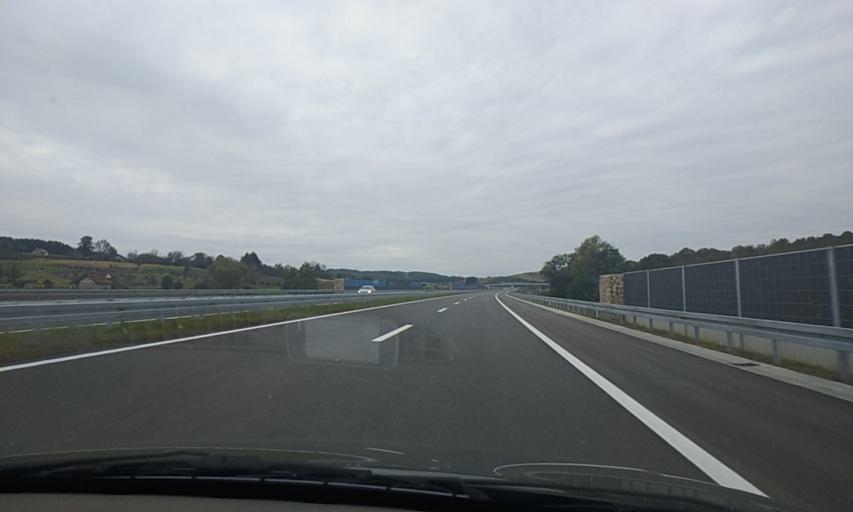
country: BA
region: Republika Srpska
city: Prnjavor
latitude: 44.8858
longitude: 17.5504
